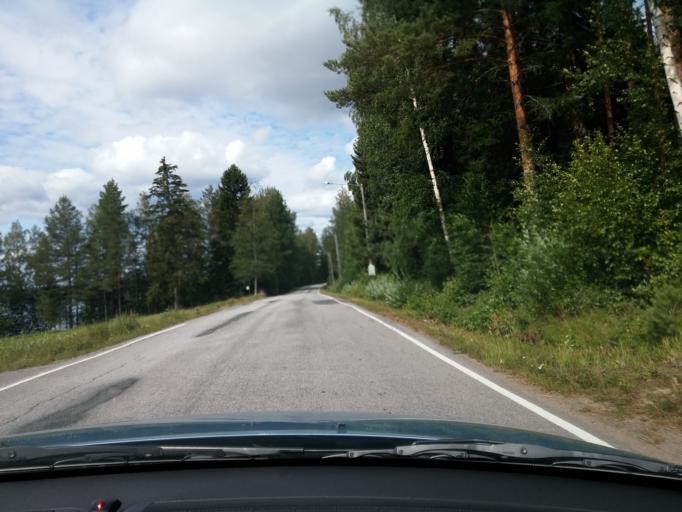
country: FI
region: Central Finland
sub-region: Saarijaervi-Viitasaari
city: Saarijaervi
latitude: 62.7212
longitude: 25.1994
